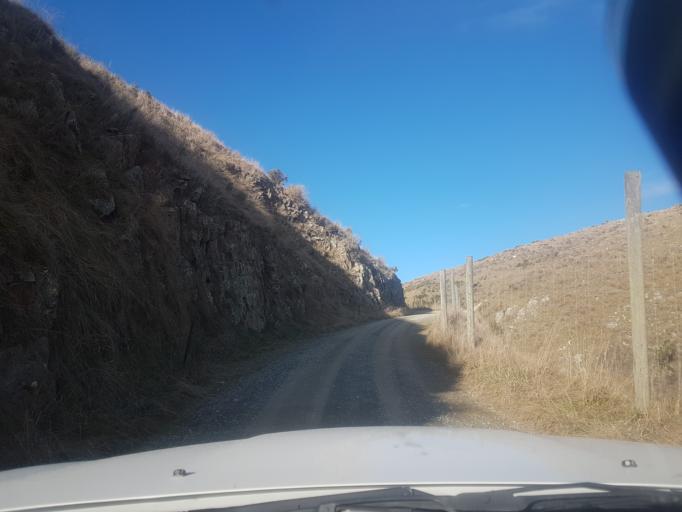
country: NZ
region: Canterbury
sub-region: Timaru District
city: Pleasant Point
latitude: -44.1740
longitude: 170.8845
